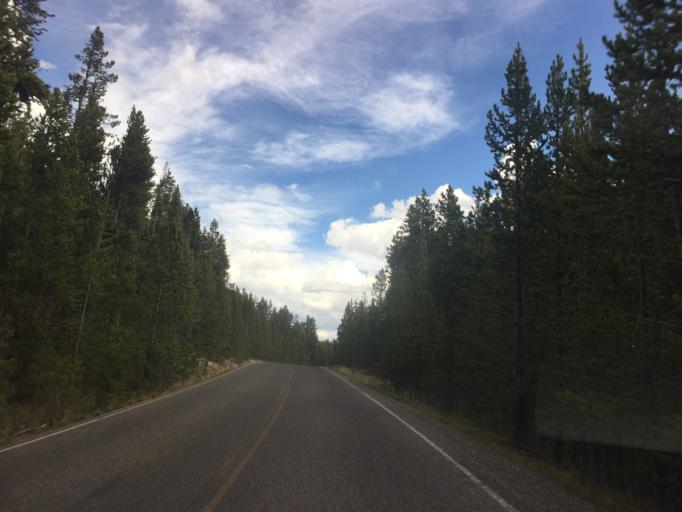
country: US
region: Montana
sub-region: Gallatin County
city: West Yellowstone
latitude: 44.7291
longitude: -110.4788
